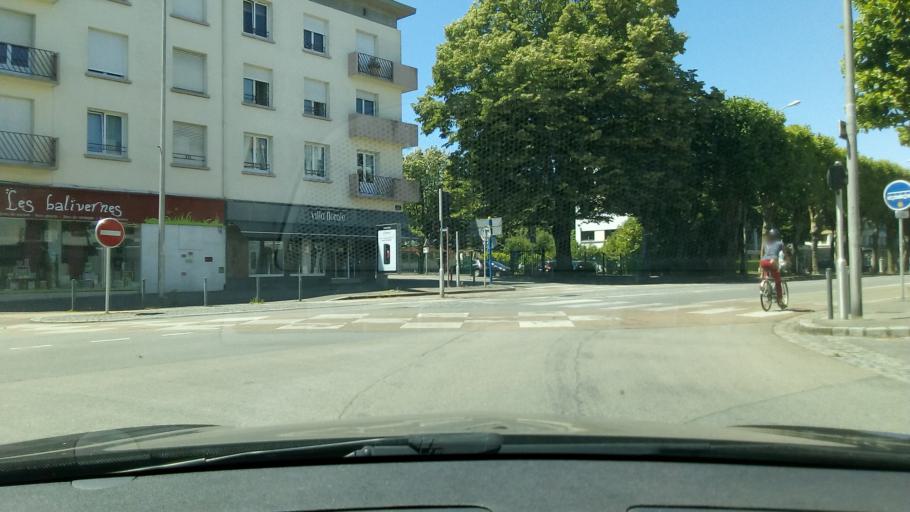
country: FR
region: Brittany
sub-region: Departement du Morbihan
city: Lorient
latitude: 47.7518
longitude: -3.3609
